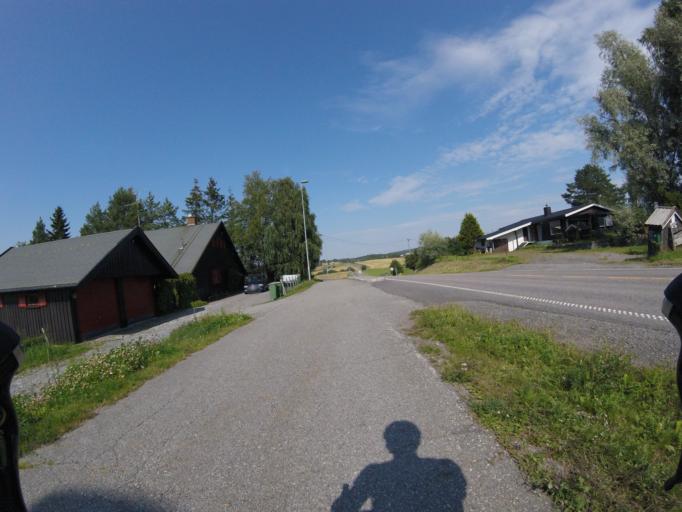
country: NO
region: Akershus
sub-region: Sorum
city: Frogner
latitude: 60.0074
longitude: 11.1065
